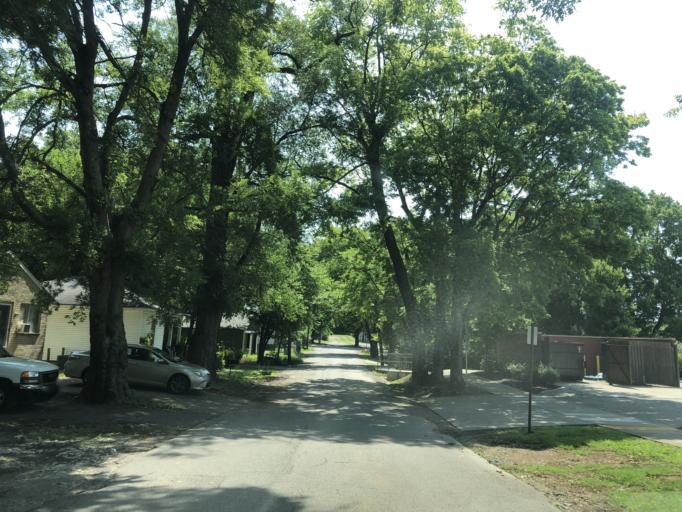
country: US
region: Tennessee
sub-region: Davidson County
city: Nashville
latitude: 36.1952
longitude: -86.7685
